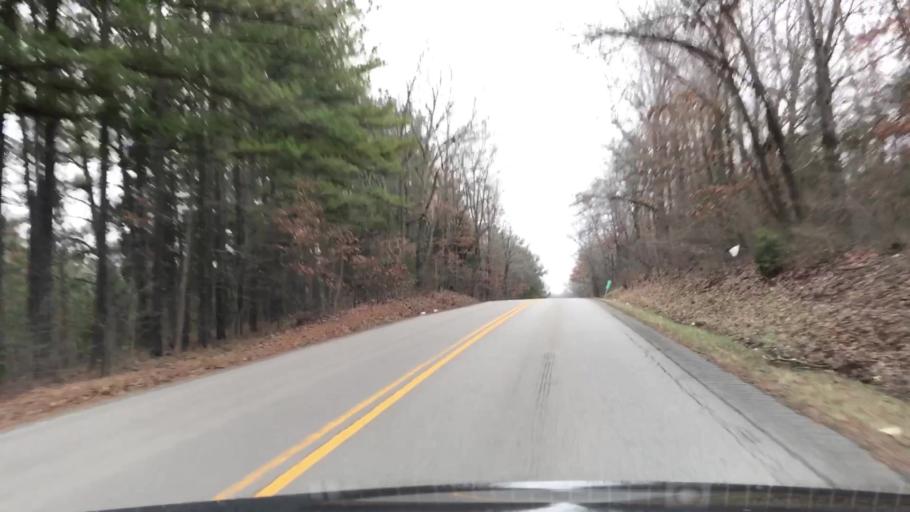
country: US
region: Kentucky
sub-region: Muhlenberg County
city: Morehead
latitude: 37.2880
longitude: -87.2106
